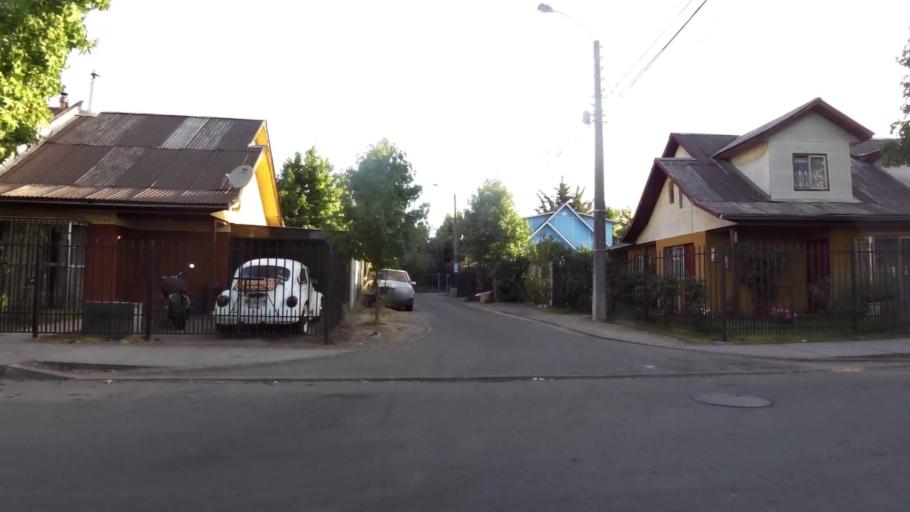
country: CL
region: Maule
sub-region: Provincia de Talca
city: Talca
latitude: -35.4482
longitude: -71.6828
